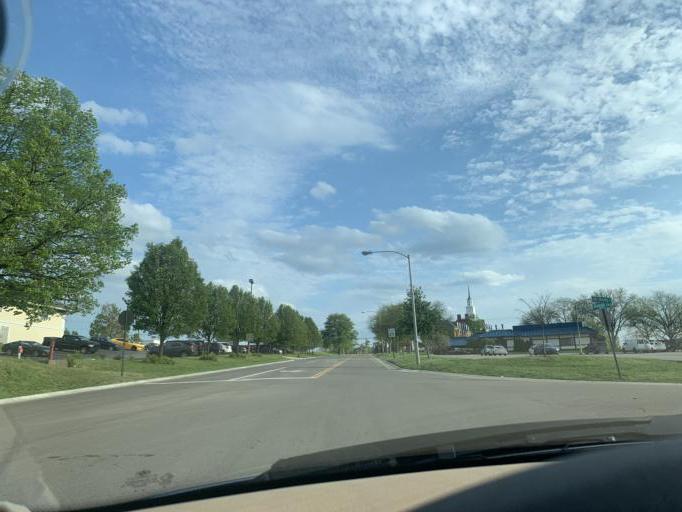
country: US
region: Ohio
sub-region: Hamilton County
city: Springdale
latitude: 39.2847
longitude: -84.4700
